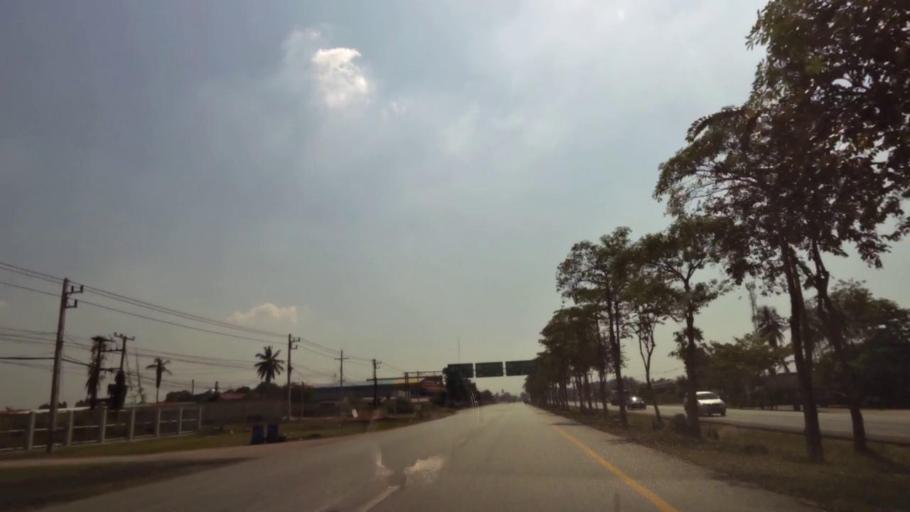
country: TH
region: Phichit
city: Bueng Na Rang
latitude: 16.1292
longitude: 100.1256
